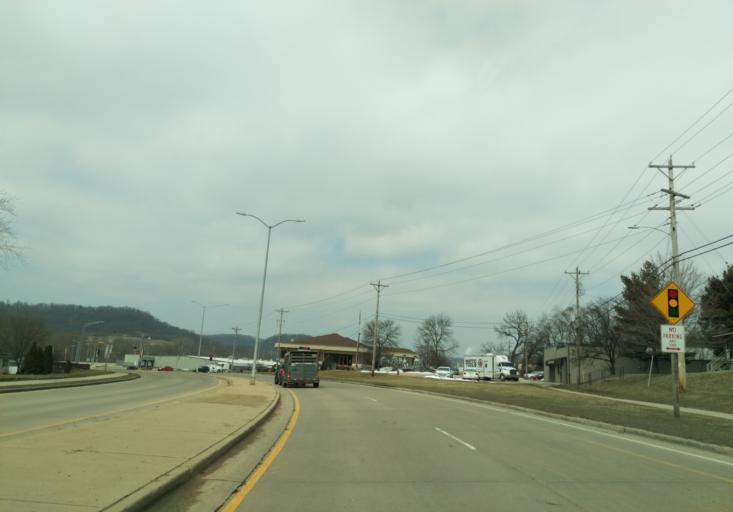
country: US
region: Wisconsin
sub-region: Richland County
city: Richland Center
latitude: 43.3239
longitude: -90.3803
